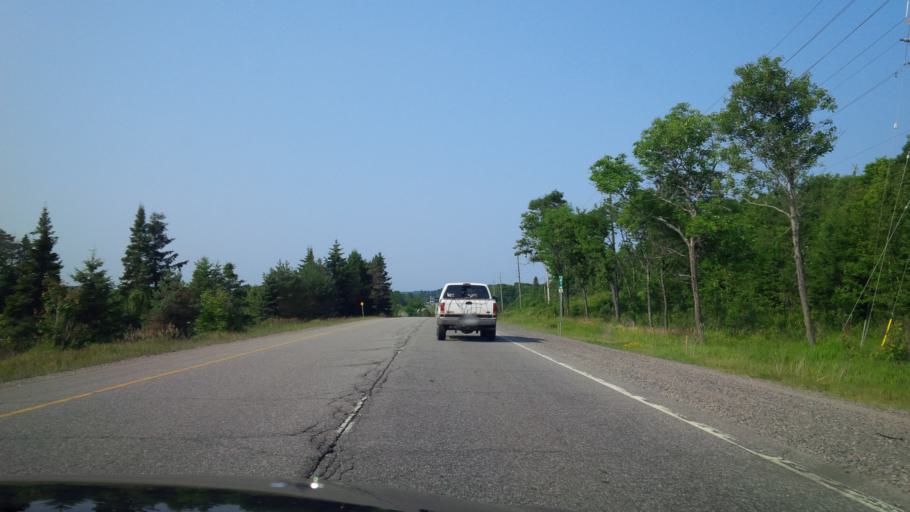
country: CA
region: Ontario
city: Huntsville
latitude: 45.2735
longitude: -79.2832
